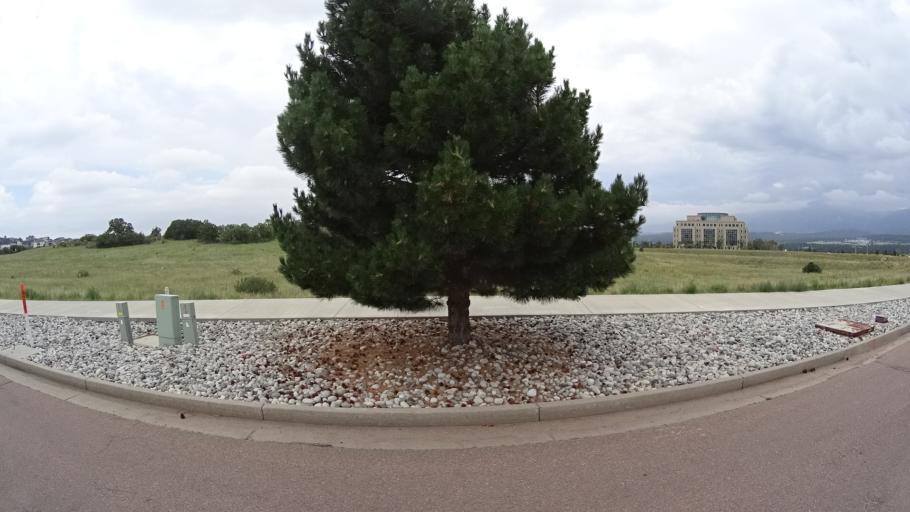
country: US
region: Colorado
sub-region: El Paso County
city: Gleneagle
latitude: 39.0102
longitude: -104.8158
